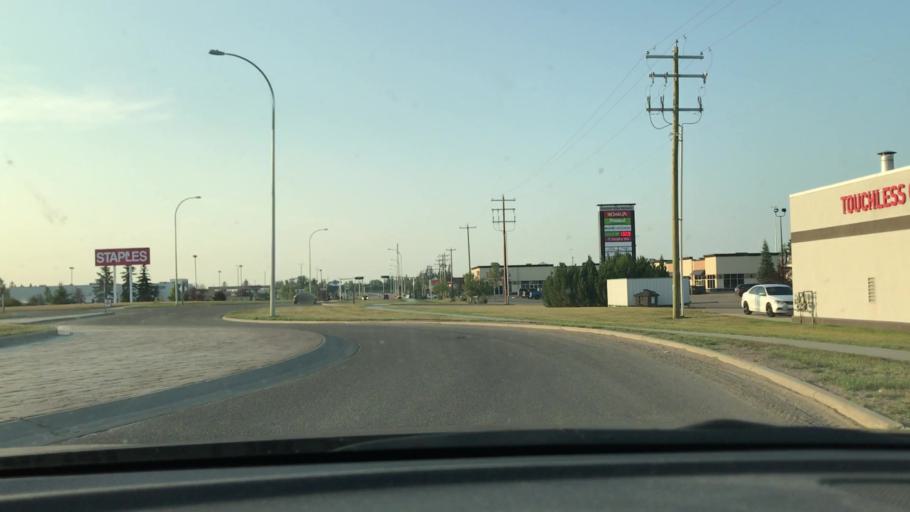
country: CA
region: Alberta
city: Red Deer
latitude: 52.2106
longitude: -113.8160
